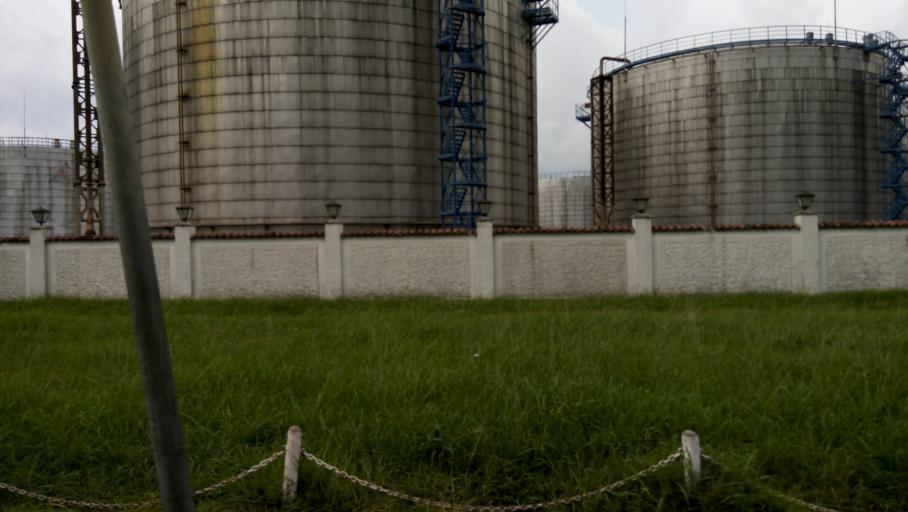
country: GE
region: Ajaria
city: Batumi
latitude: 41.6421
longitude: 41.6613
